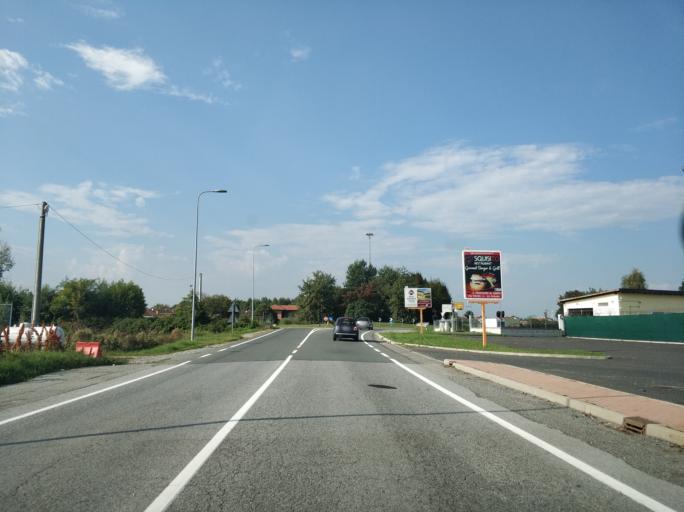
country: IT
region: Piedmont
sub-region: Provincia di Torino
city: San Maurizio
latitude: 45.2043
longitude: 7.6367
